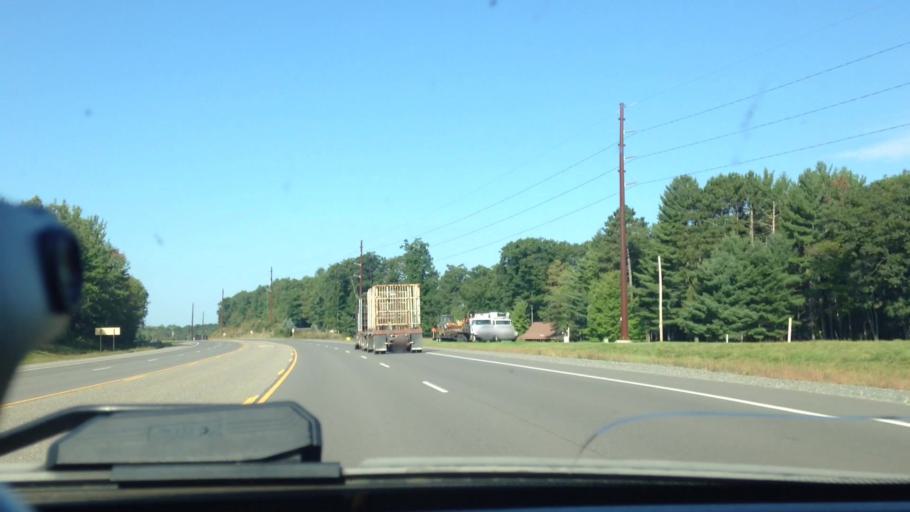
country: US
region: Michigan
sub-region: Dickinson County
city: Iron Mountain
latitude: 45.8820
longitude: -88.1309
